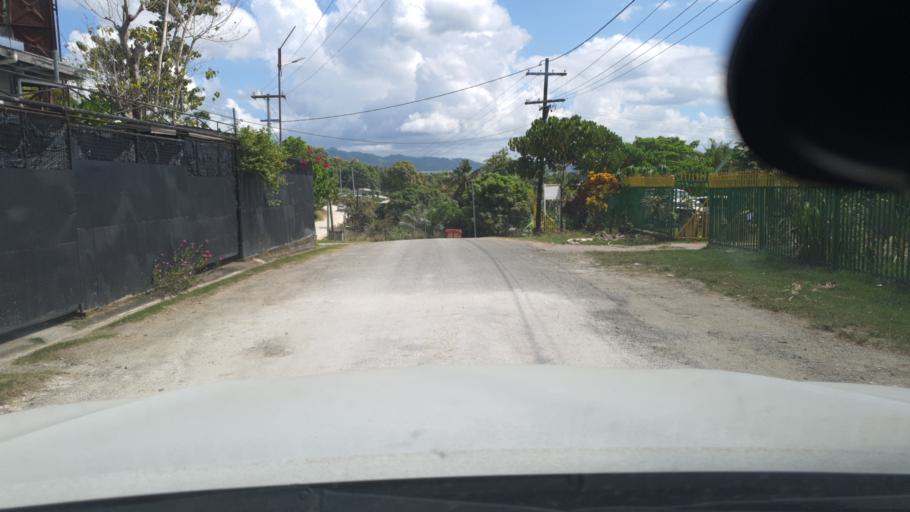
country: SB
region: Guadalcanal
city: Honiara
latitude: -9.4302
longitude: 159.9370
